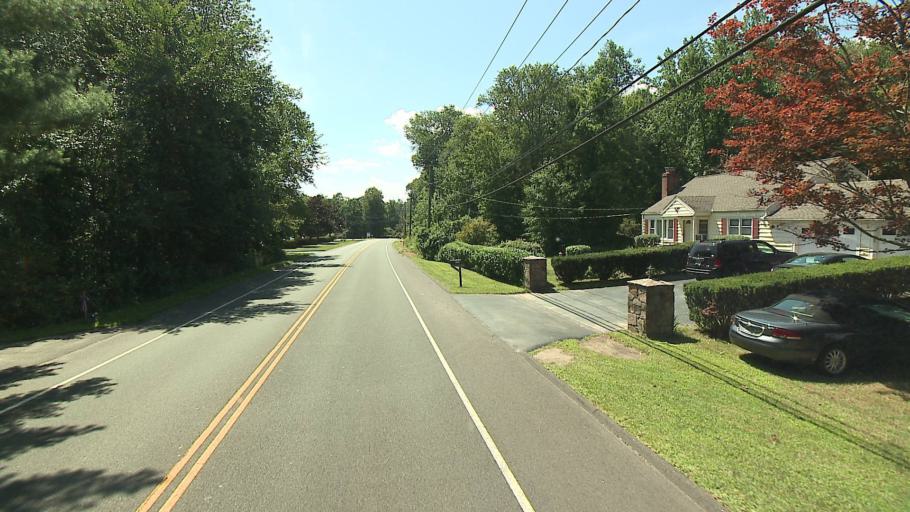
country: US
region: Connecticut
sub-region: Fairfield County
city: Trumbull
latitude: 41.3223
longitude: -73.2113
